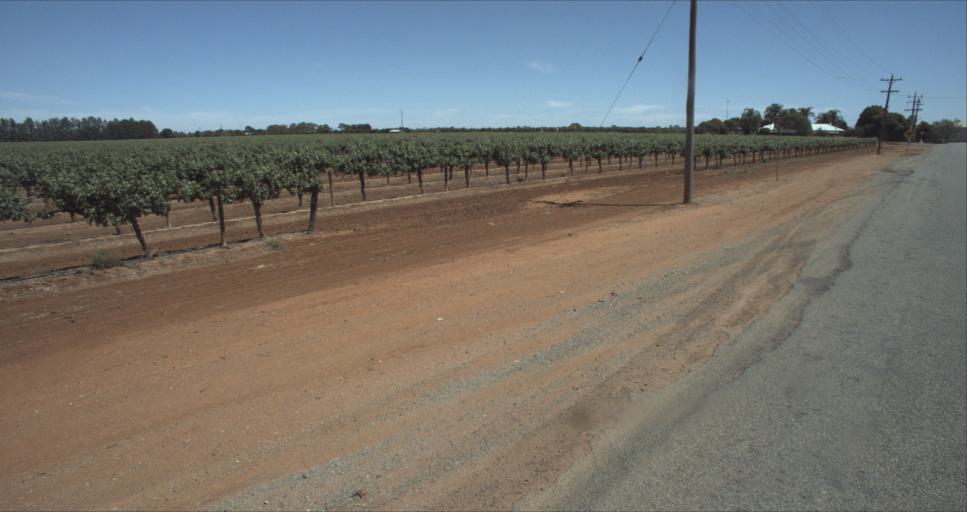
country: AU
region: New South Wales
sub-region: Leeton
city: Leeton
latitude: -34.5308
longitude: 146.3309
